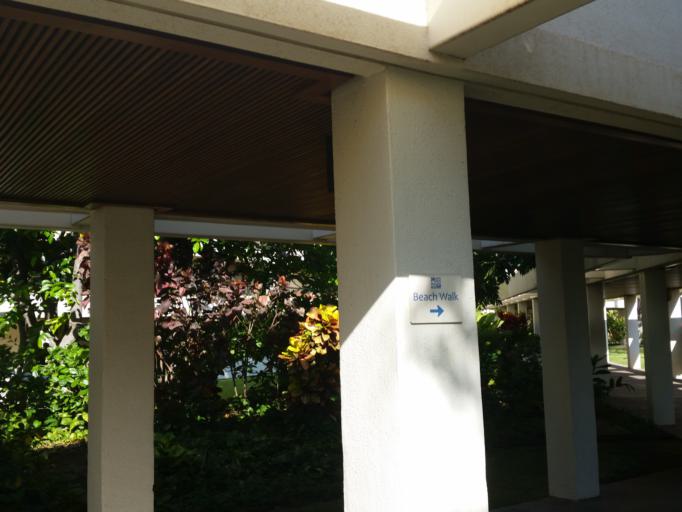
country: US
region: Hawaii
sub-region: Maui County
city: Ka'anapali
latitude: 20.9272
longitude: -156.6941
